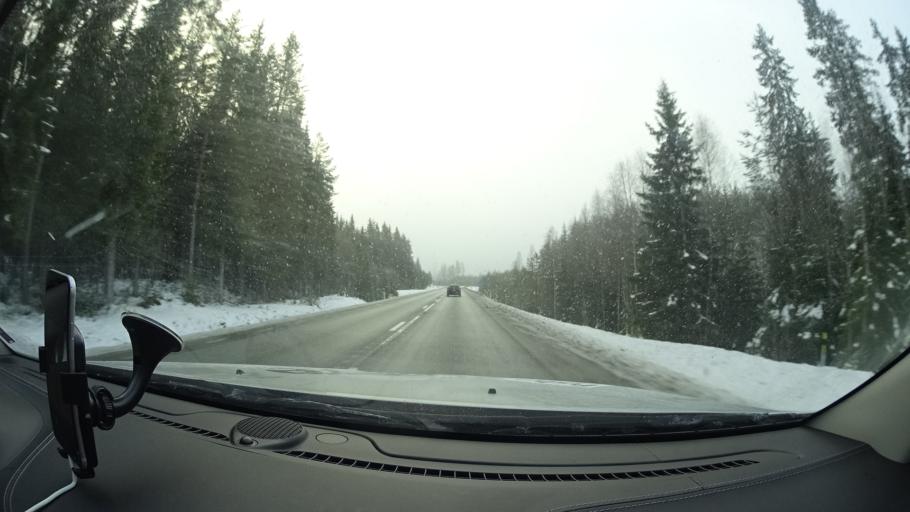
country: SE
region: OErebro
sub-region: Ljusnarsbergs Kommun
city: Kopparberg
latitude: 59.8974
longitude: 15.0183
